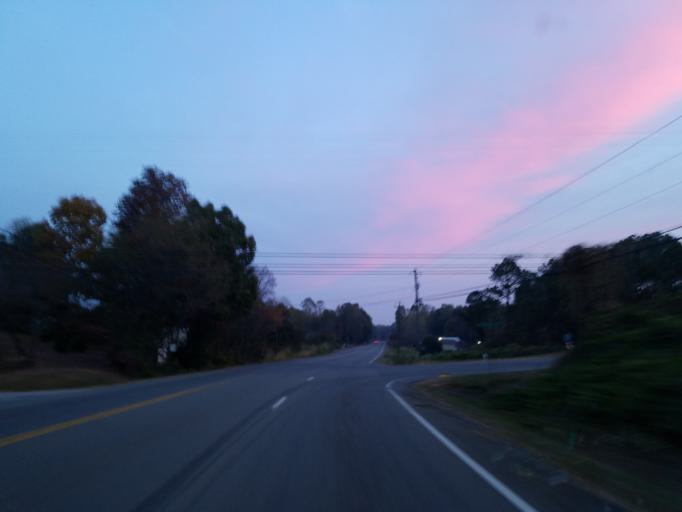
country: US
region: Georgia
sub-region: Pickens County
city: Jasper
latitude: 34.4896
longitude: -84.4604
